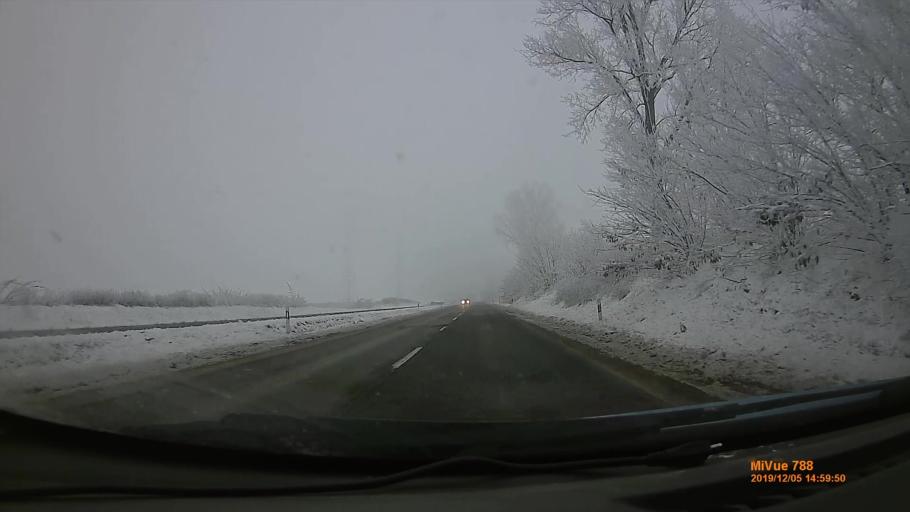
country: HU
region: Szabolcs-Szatmar-Bereg
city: Tiszanagyfalu
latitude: 48.0603
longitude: 21.5509
